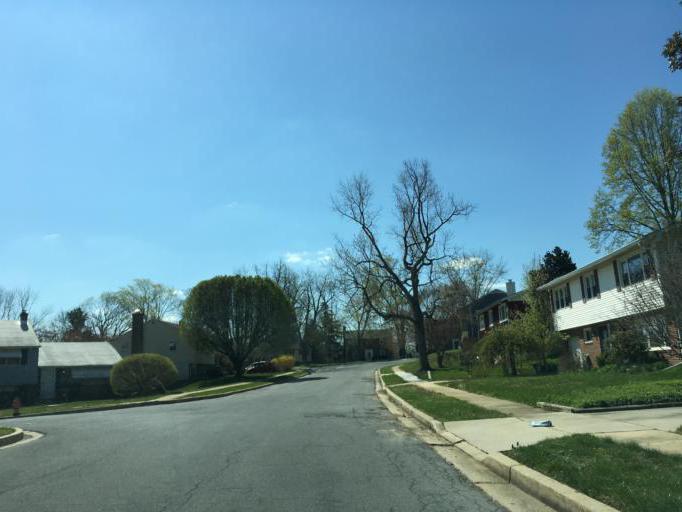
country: US
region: Maryland
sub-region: Baltimore County
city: Lutherville
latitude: 39.4212
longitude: -76.6102
